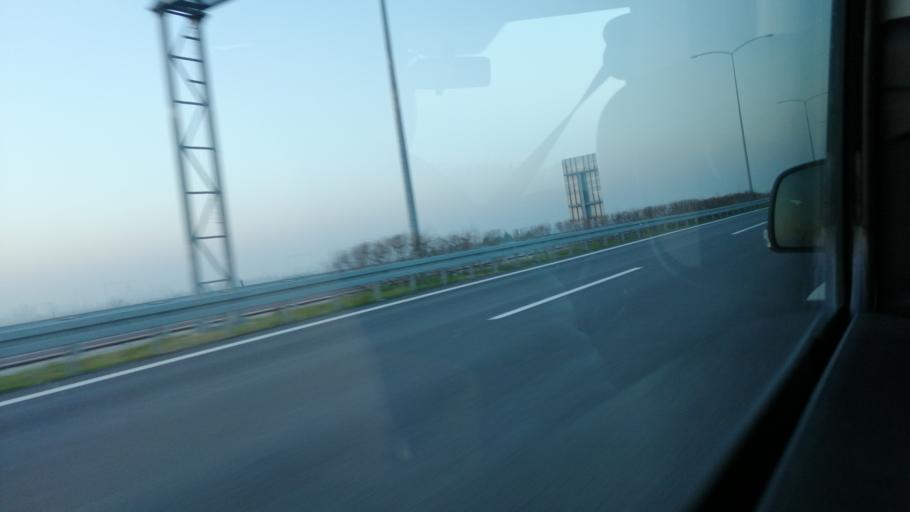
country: TR
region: Yalova
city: Altinova
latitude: 40.7049
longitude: 29.4926
